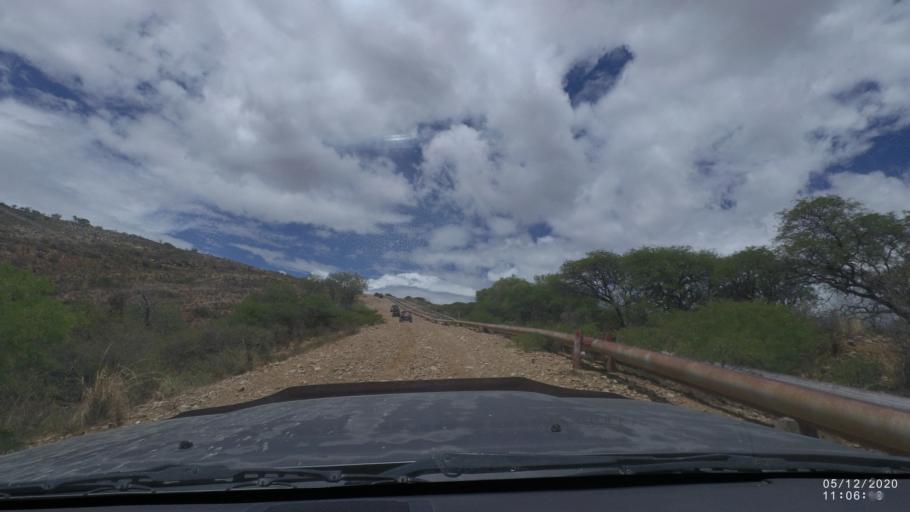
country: BO
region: Cochabamba
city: Sipe Sipe
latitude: -17.5501
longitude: -66.3060
